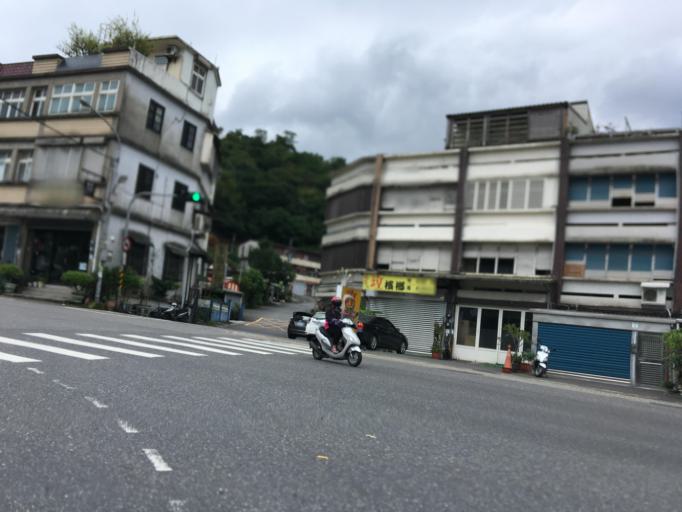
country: TW
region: Taiwan
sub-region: Yilan
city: Yilan
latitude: 24.6158
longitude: 121.8110
